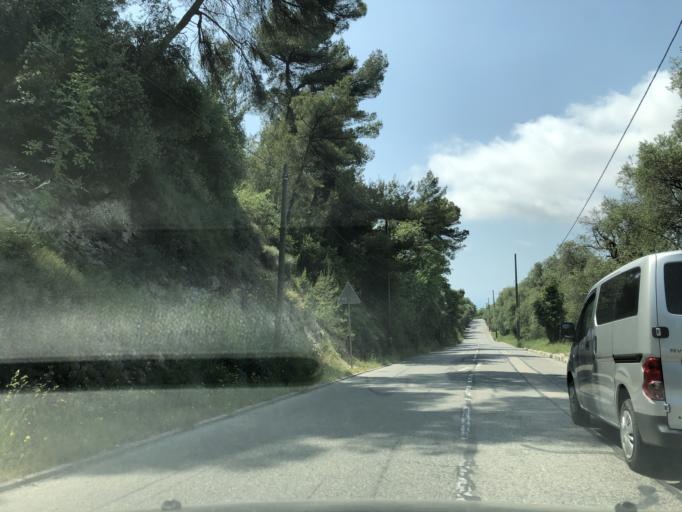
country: FR
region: Provence-Alpes-Cote d'Azur
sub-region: Departement des Alpes-Maritimes
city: Saint-Andre-de-la-Roche
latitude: 43.7297
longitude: 7.2959
